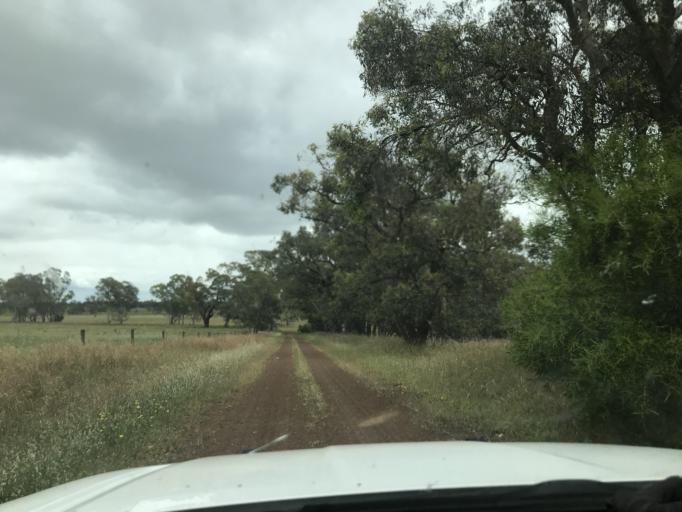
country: AU
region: South Australia
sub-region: Wattle Range
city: Penola
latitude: -37.0979
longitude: 141.2701
